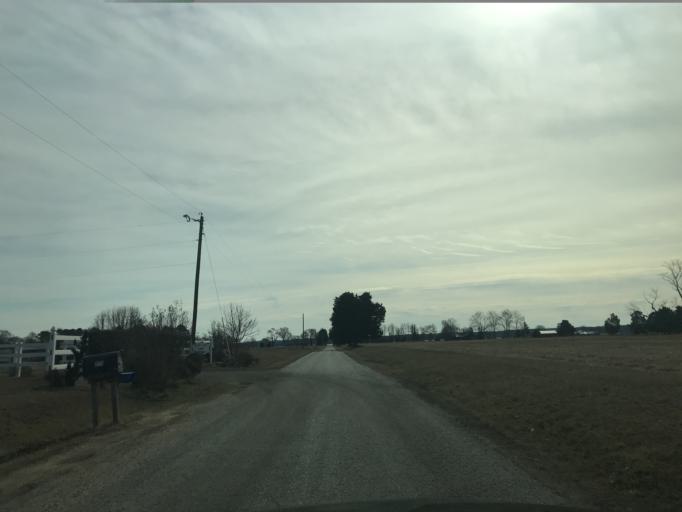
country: US
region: Virginia
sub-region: King George County
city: Dahlgren
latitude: 38.3909
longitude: -77.1504
